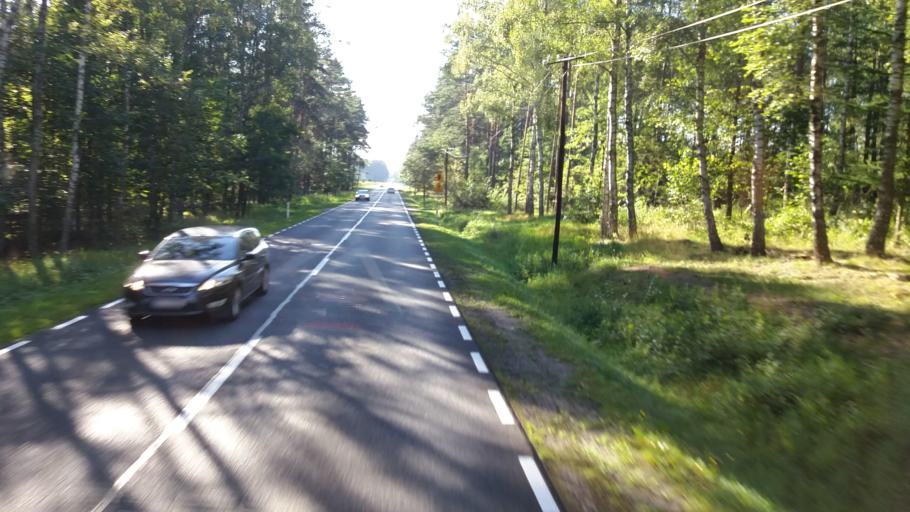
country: PL
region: West Pomeranian Voivodeship
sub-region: Powiat drawski
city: Kalisz Pomorski
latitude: 53.2995
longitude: 15.8146
